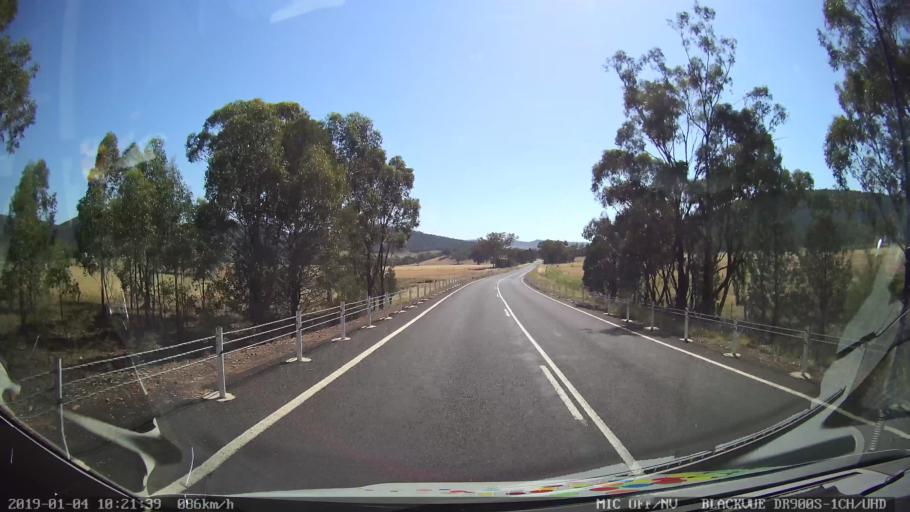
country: AU
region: New South Wales
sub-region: Cabonne
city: Canowindra
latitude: -33.3715
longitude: 148.5132
